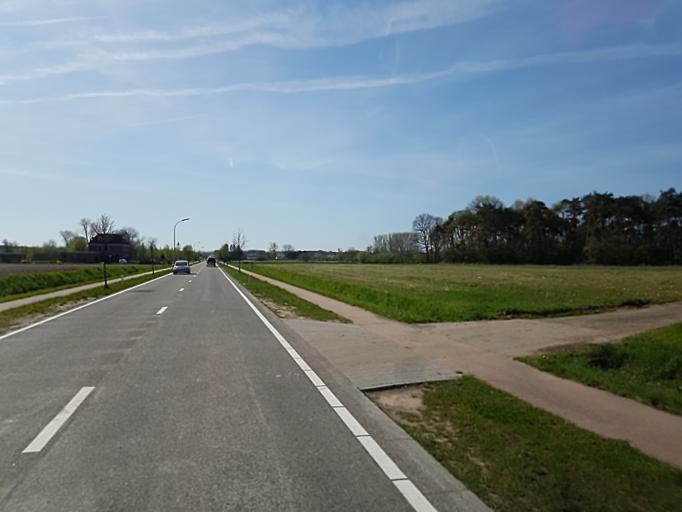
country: BE
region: Flanders
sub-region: Provincie Antwerpen
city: Westerlo
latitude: 51.1100
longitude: 4.9437
